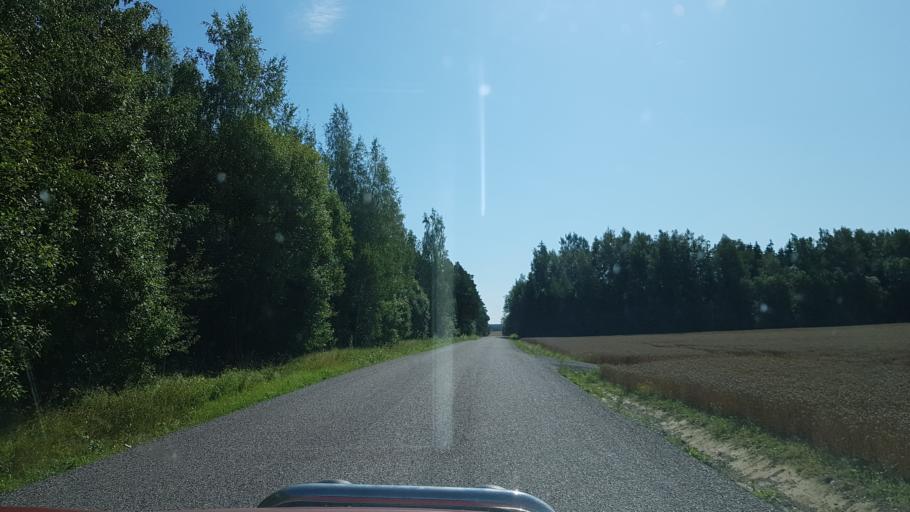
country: EE
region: Tartu
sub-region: Puhja vald
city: Puhja
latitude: 58.2554
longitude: 26.3257
